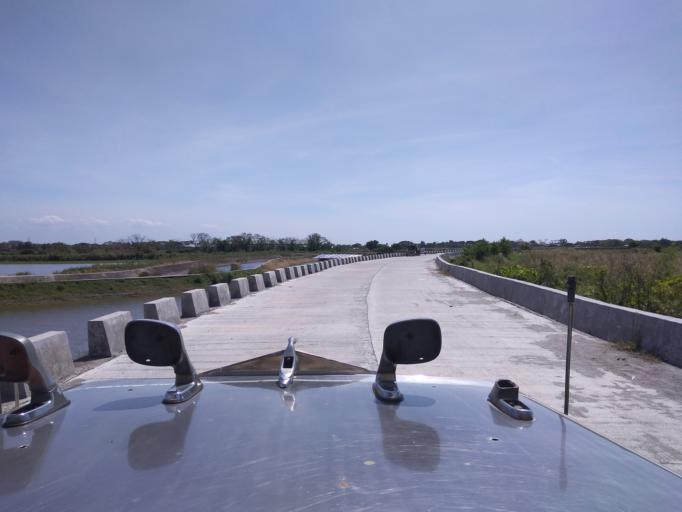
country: PH
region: Central Luzon
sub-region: Province of Pampanga
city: Minalin
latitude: 14.9884
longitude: 120.6943
